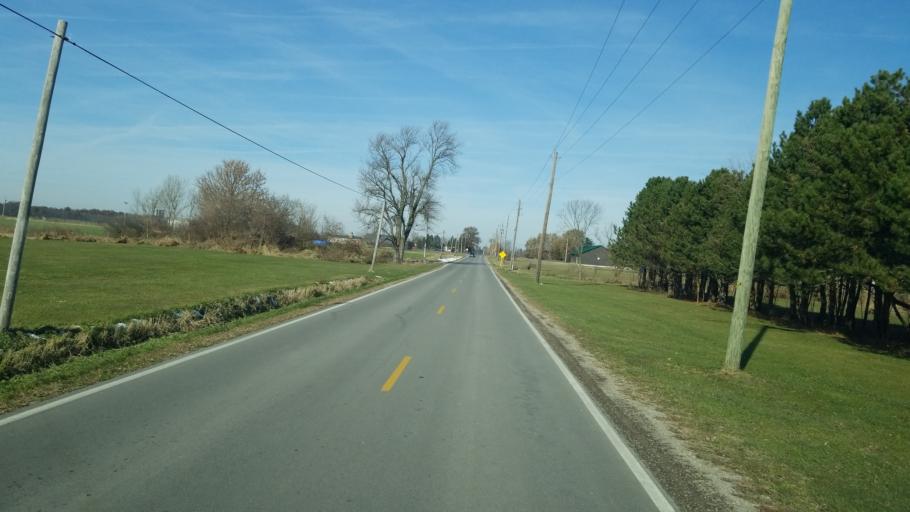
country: US
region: Ohio
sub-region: Huron County
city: Wakeman
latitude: 41.2441
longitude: -82.4222
